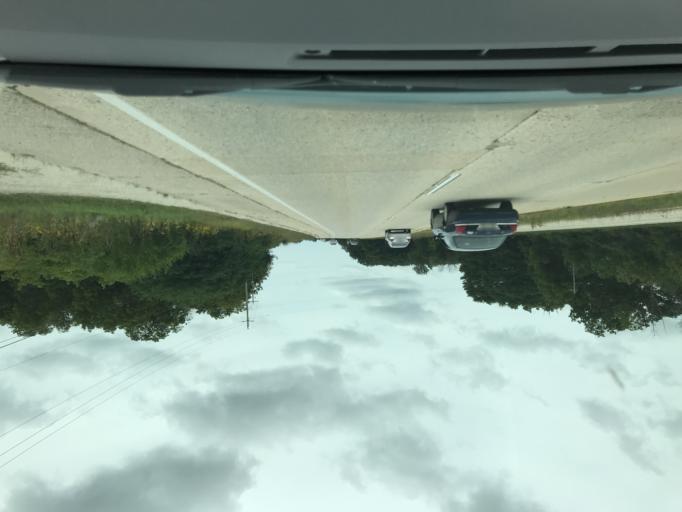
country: US
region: Wisconsin
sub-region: Kenosha County
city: Bristol
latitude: 42.5681
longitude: -88.0610
